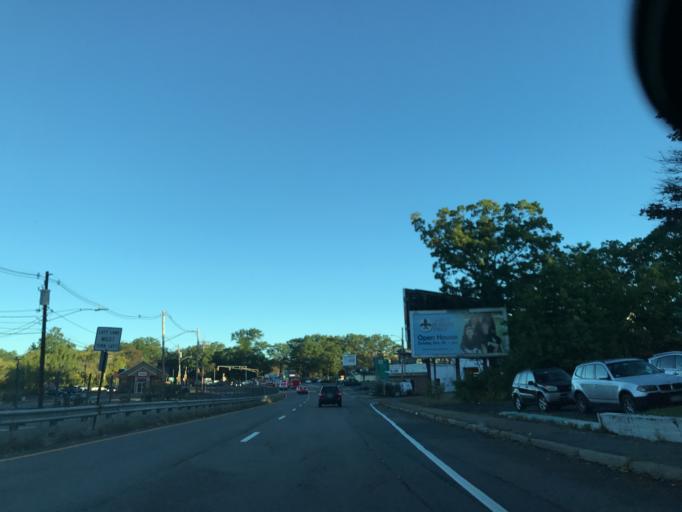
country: US
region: Massachusetts
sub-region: Norfolk County
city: Dedham
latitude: 42.2697
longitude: -71.1720
